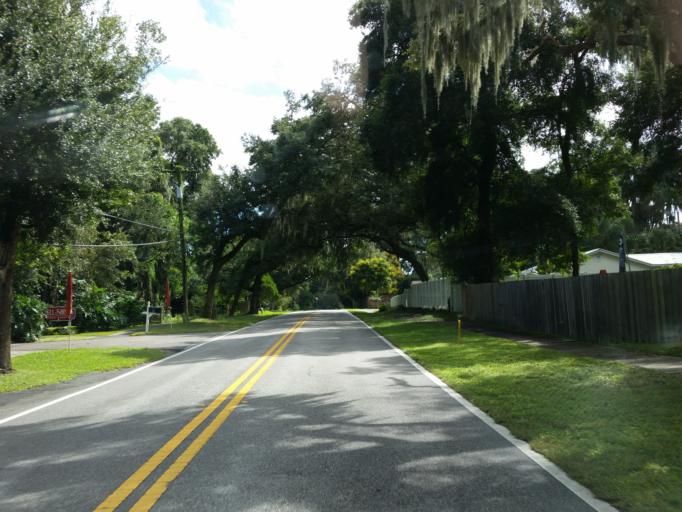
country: US
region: Florida
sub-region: Hillsborough County
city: Brandon
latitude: 27.9198
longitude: -82.2694
